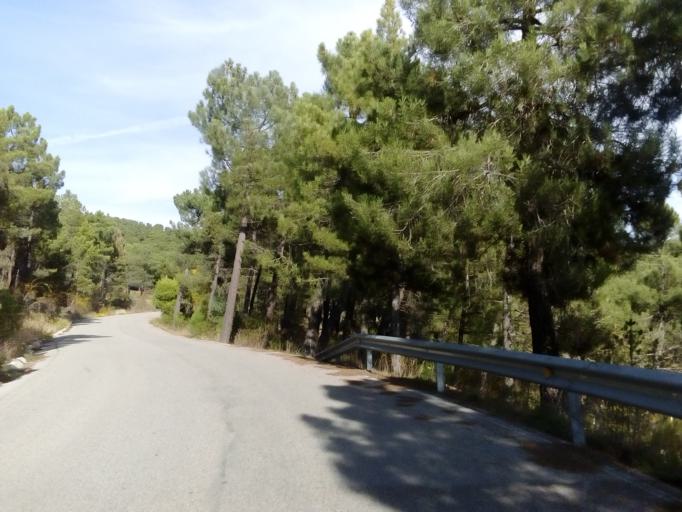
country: ES
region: Catalonia
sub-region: Provincia de Lleida
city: Bellver de Cerdanya
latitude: 42.3754
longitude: 1.7934
